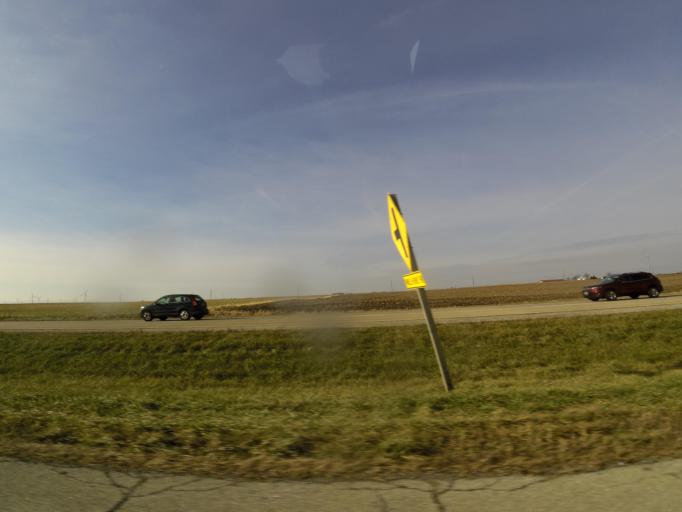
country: US
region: Illinois
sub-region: Macon County
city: Maroa
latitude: 40.0711
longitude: -88.9656
